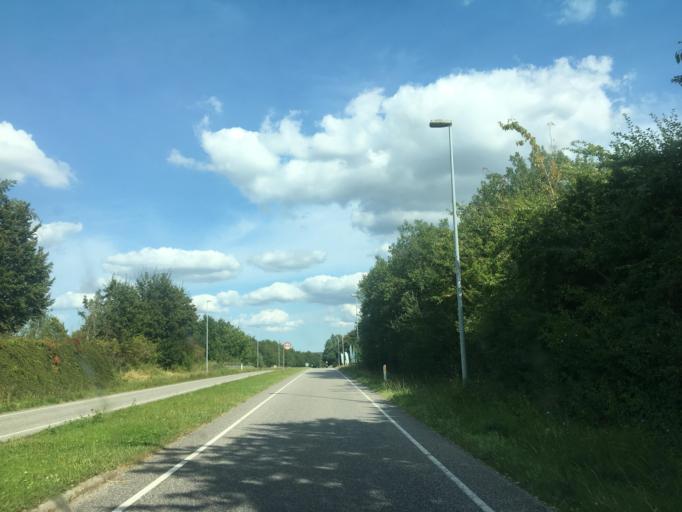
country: DK
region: South Denmark
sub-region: Middelfart Kommune
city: Ejby
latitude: 55.4007
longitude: 9.9725
